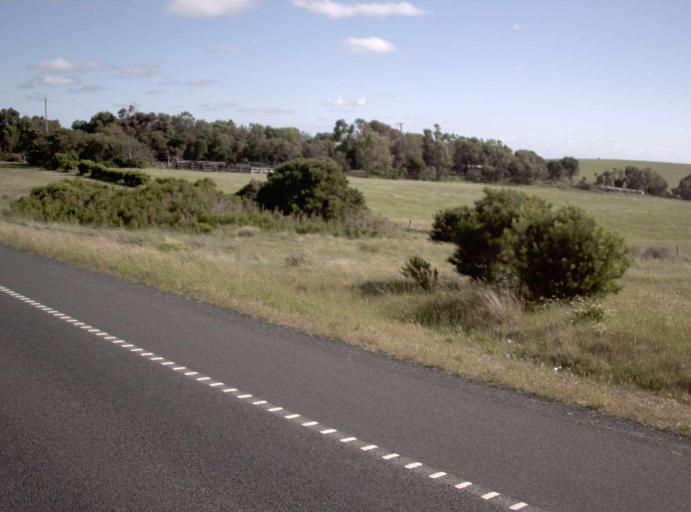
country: AU
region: Victoria
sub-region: Bass Coast
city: North Wonthaggi
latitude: -38.5392
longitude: 145.4578
